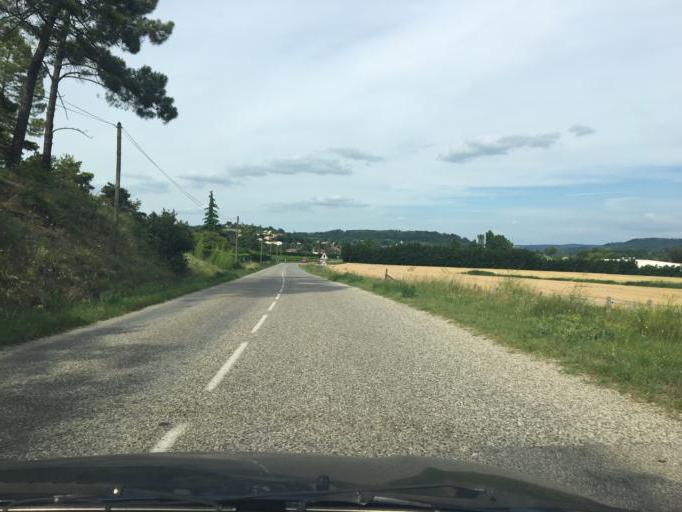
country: FR
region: Rhone-Alpes
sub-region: Departement de la Drome
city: Clerieux
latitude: 45.1143
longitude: 4.9626
